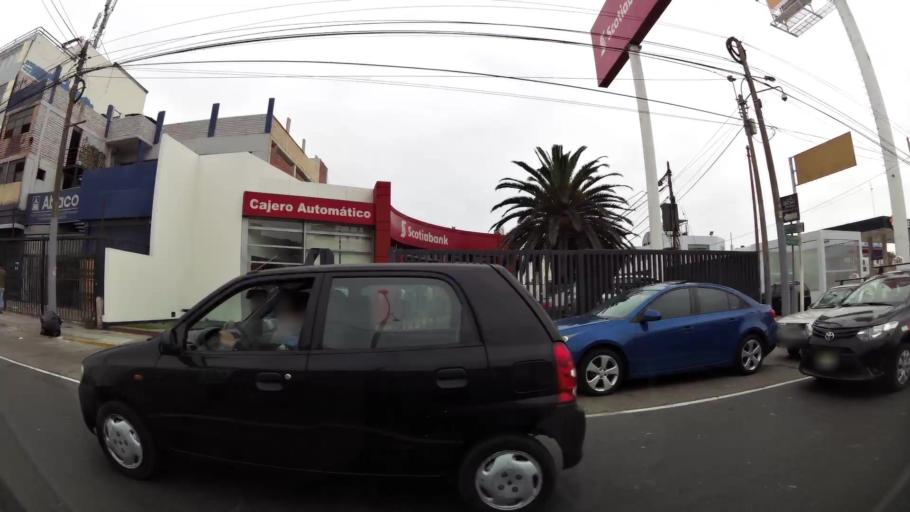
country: PE
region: Callao
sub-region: Callao
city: Callao
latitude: -12.0778
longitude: -77.0927
